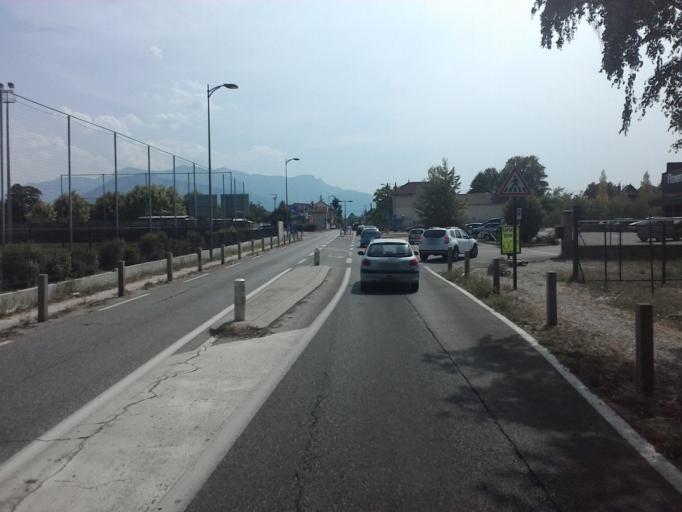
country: FR
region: Rhone-Alpes
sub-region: Departement de l'Isere
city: Voiron
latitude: 45.3542
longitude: 5.5981
